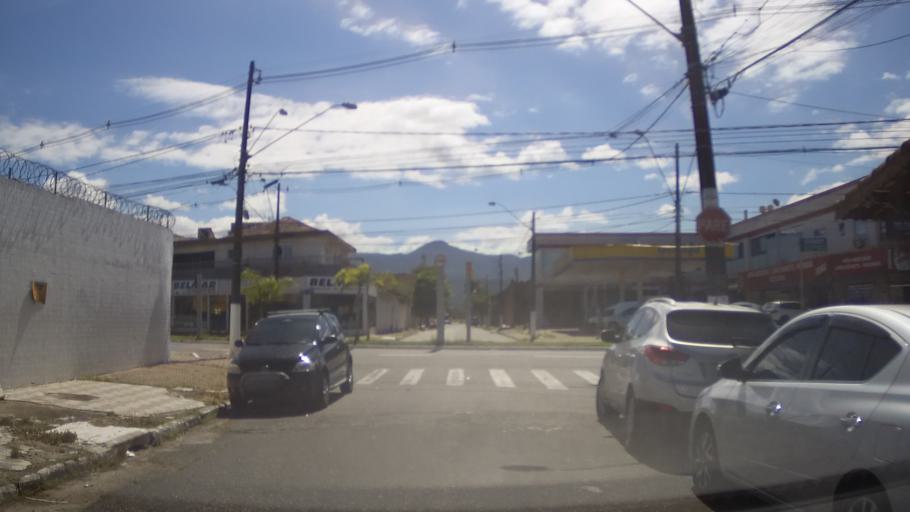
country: BR
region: Sao Paulo
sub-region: Praia Grande
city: Praia Grande
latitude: -24.0355
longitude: -46.5037
